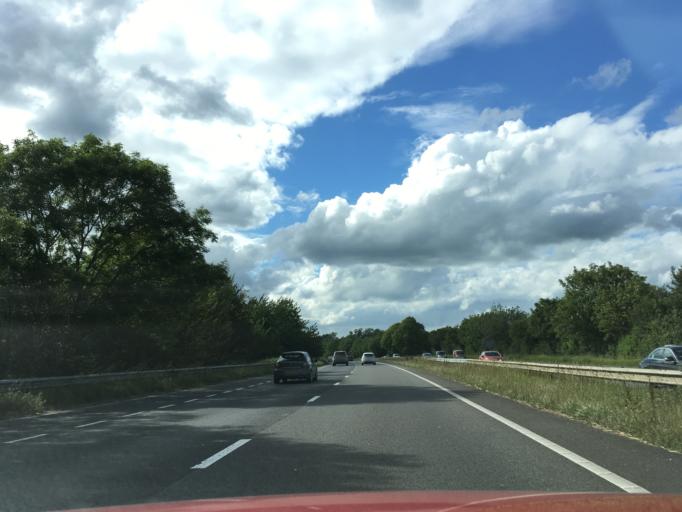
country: GB
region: England
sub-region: Oxfordshire
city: Wheatley
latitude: 51.7536
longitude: -1.1419
